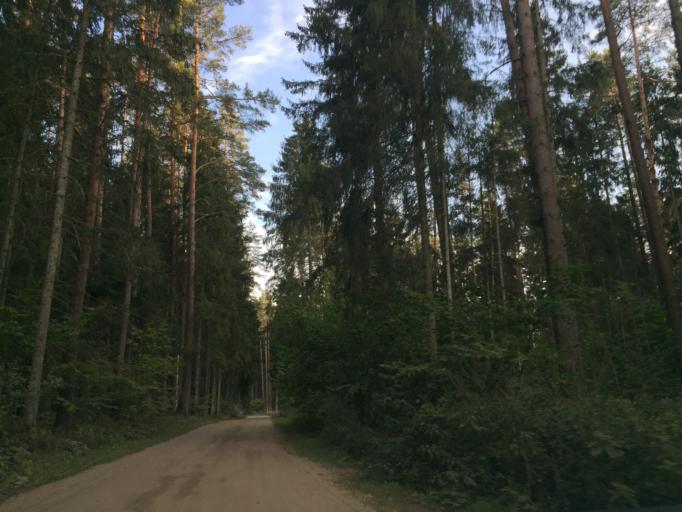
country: LV
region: Baldone
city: Baldone
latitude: 56.7683
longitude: 24.4045
